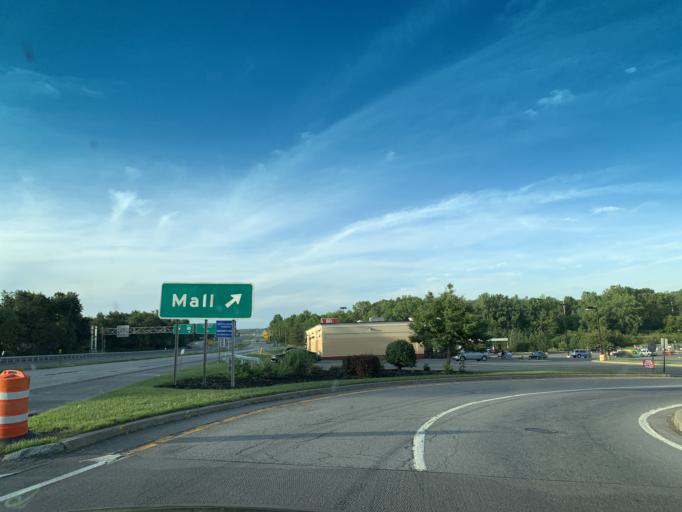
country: US
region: New York
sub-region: Oneida County
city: Utica
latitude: 43.1278
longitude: -75.2256
